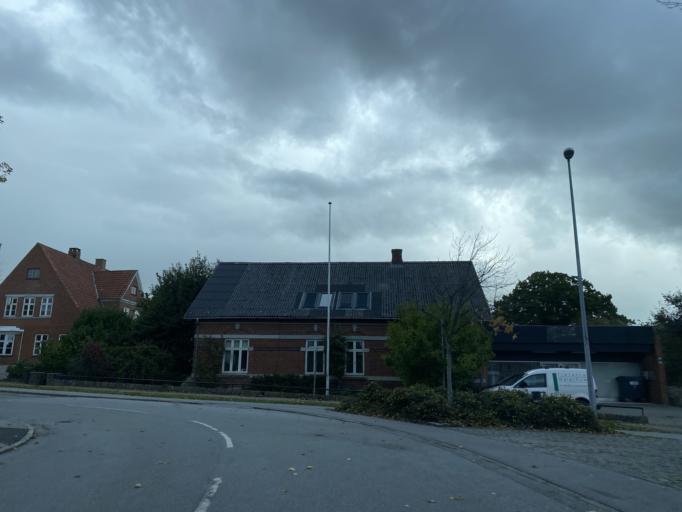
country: DK
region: South Denmark
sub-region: Haderslev Kommune
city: Haderslev
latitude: 55.2453
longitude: 9.4991
